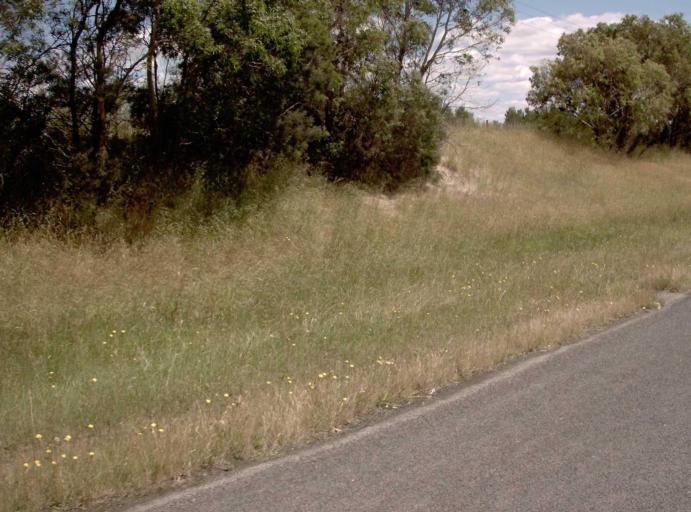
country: AU
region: Victoria
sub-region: Cardinia
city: Koo-Wee-Rup
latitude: -38.2935
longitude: 145.5448
